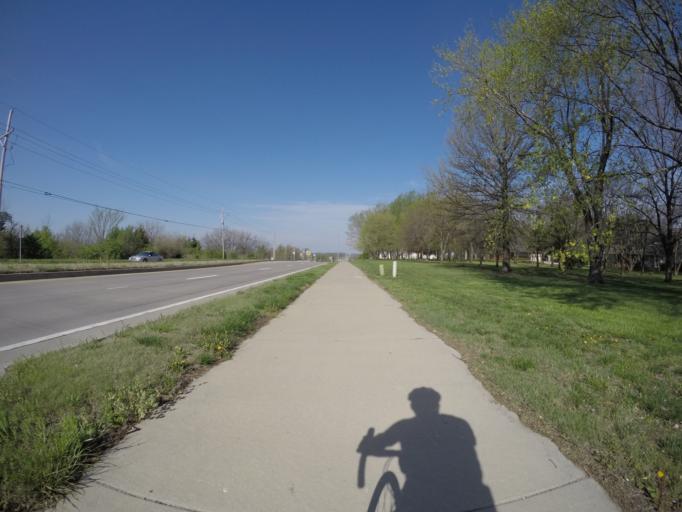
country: US
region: Missouri
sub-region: Cass County
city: Raymore
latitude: 38.8545
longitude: -94.4389
